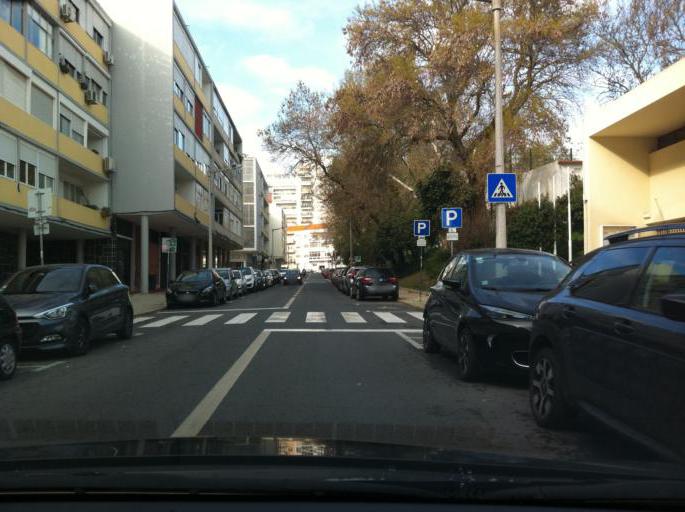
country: PT
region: Lisbon
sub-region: Lisbon
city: Lisbon
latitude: 38.7463
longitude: -9.1366
